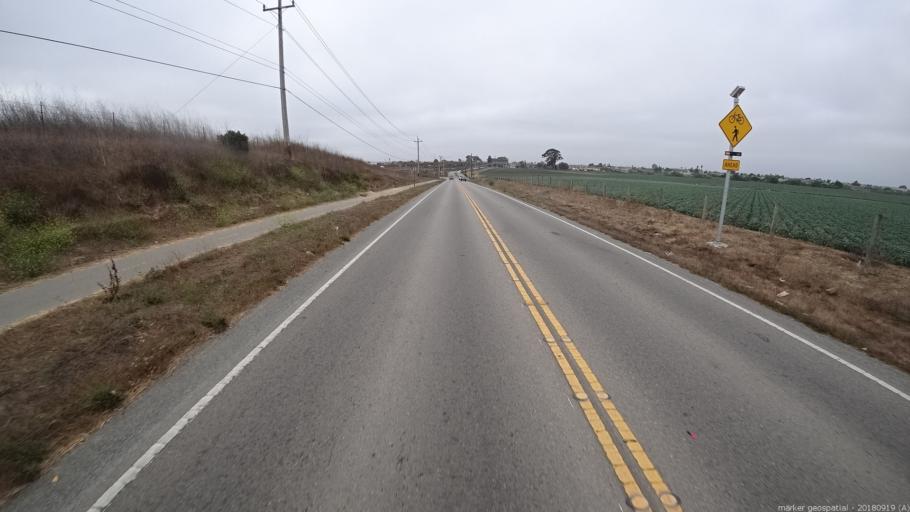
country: US
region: California
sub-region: Monterey County
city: Castroville
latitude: 36.7717
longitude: -121.7424
